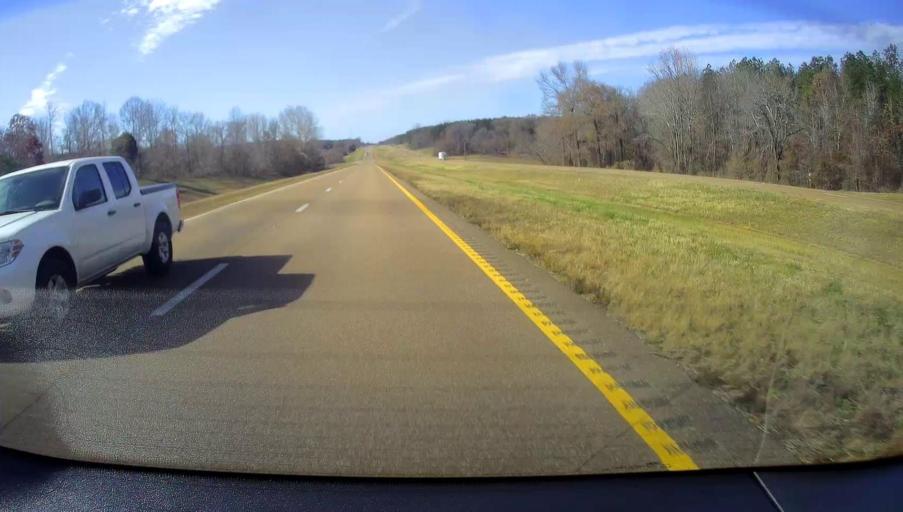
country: US
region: Mississippi
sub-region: Benton County
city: Ashland
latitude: 34.9488
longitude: -89.1008
